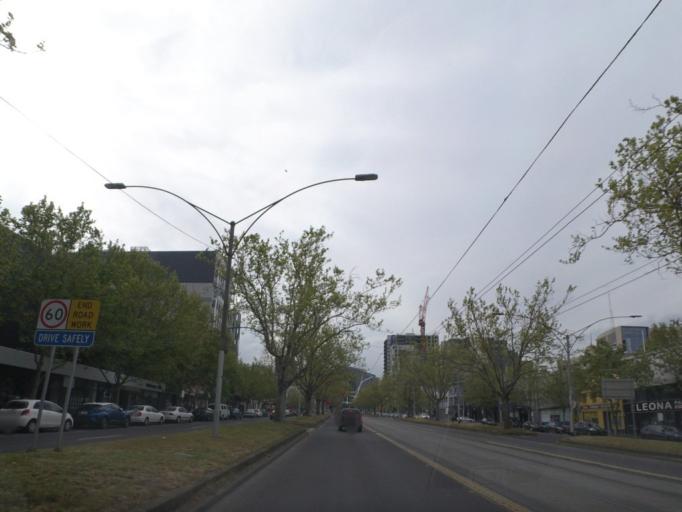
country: AU
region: Victoria
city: Carlton
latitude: -37.8053
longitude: 144.9590
